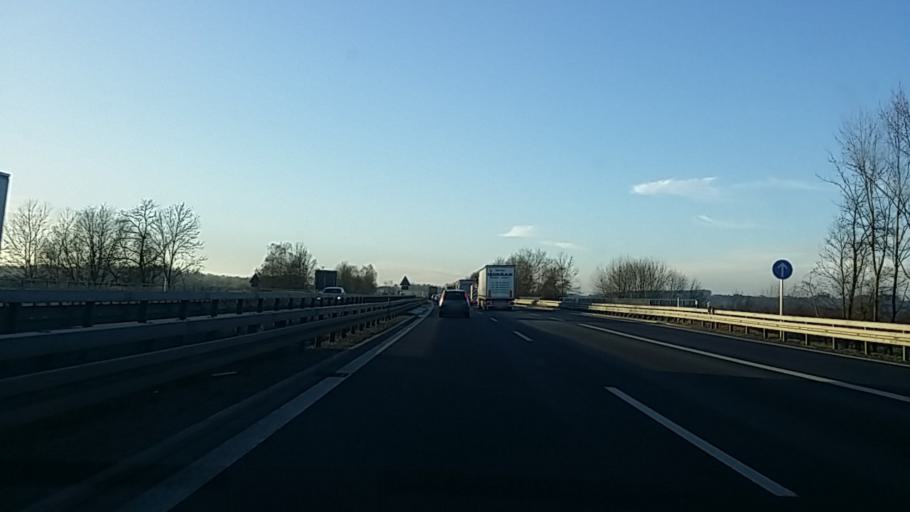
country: DE
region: Bavaria
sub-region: Lower Bavaria
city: Windberg
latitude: 48.9213
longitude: 12.7334
